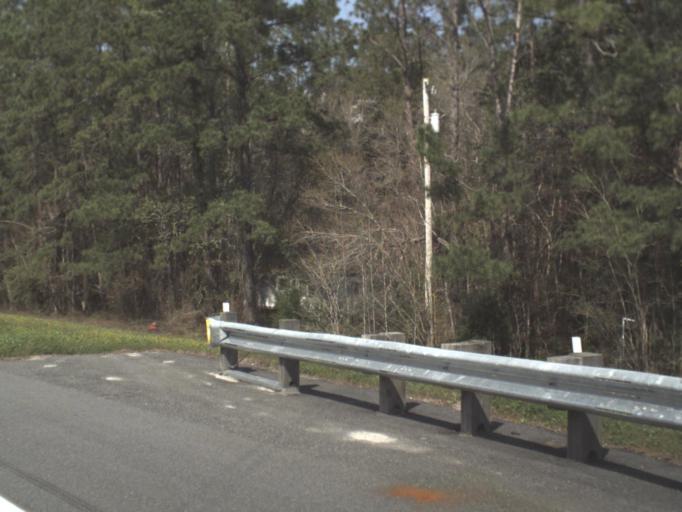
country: US
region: Florida
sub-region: Franklin County
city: Carrabelle
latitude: 29.9893
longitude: -84.5025
